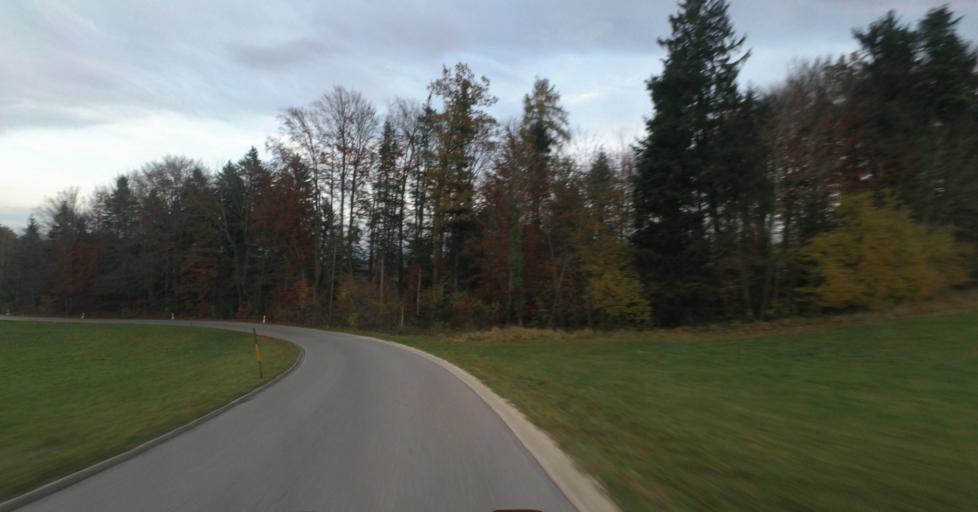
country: DE
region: Bavaria
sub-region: Upper Bavaria
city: Prien am Chiemsee
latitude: 47.8412
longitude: 12.3174
